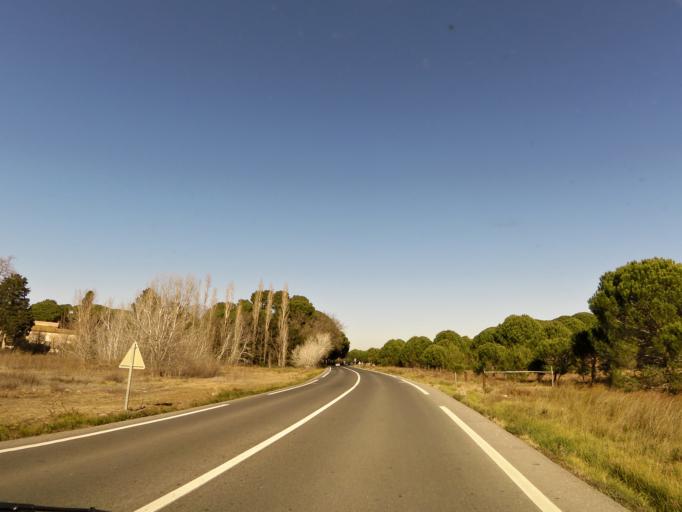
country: FR
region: Languedoc-Roussillon
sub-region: Departement du Gard
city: Aigues-Mortes
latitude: 43.5833
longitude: 4.2081
